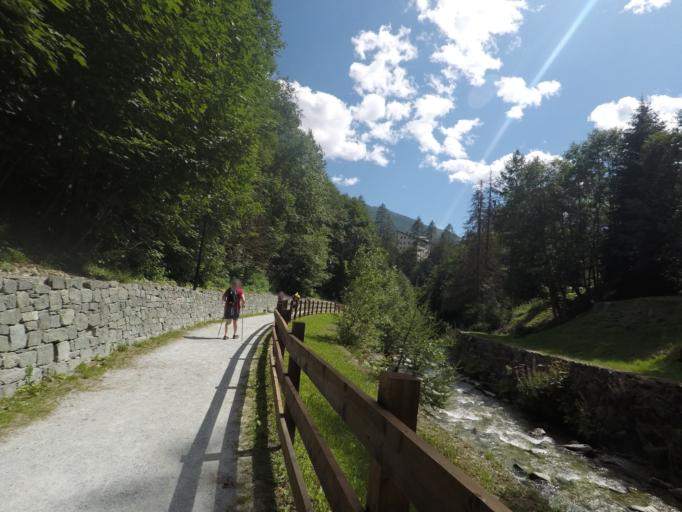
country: IT
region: Aosta Valley
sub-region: Valle d'Aosta
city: Paquier
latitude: 45.8829
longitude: 7.6229
